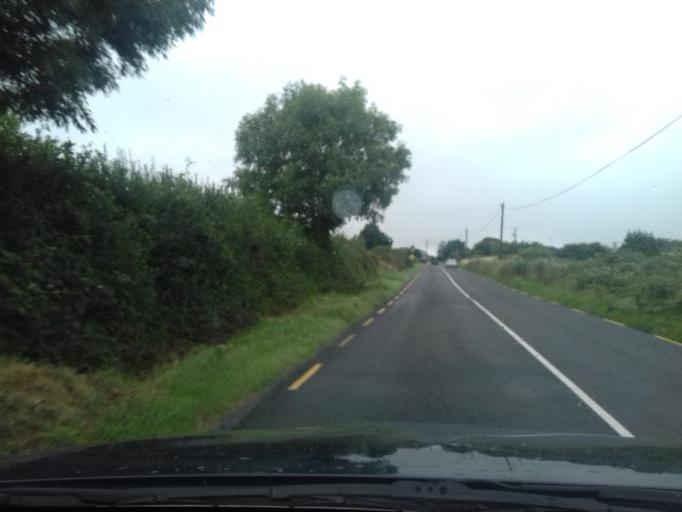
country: IE
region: Leinster
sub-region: County Carlow
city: Bagenalstown
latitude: 52.6267
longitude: -6.9422
